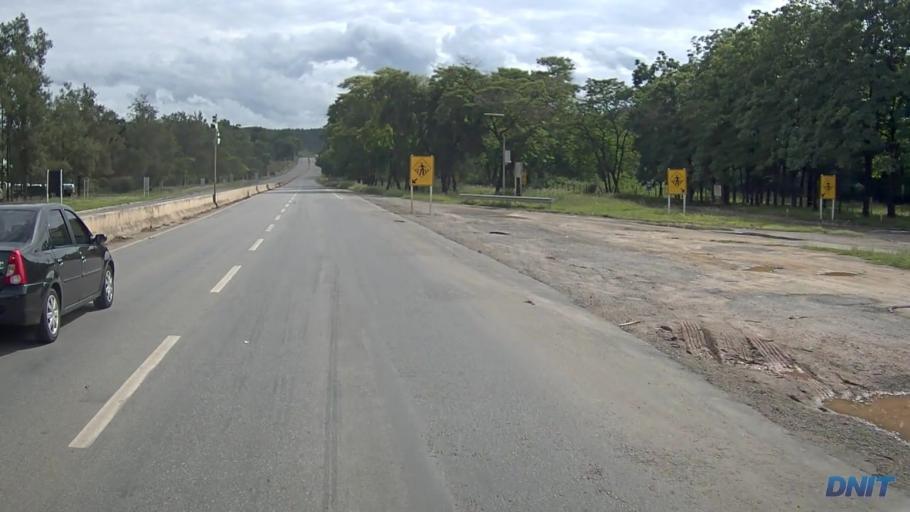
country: BR
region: Minas Gerais
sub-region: Ipaba
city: Ipaba
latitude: -19.3139
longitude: -42.3977
